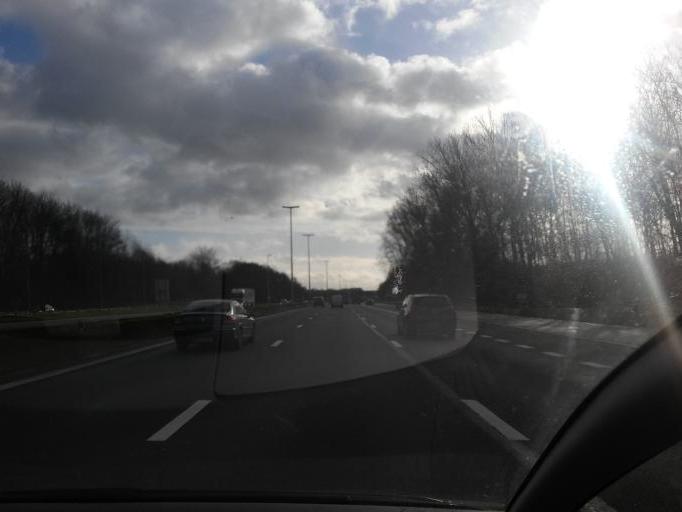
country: BE
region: Wallonia
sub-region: Province du Brabant Wallon
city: Wavre
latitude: 50.6970
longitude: 4.6179
